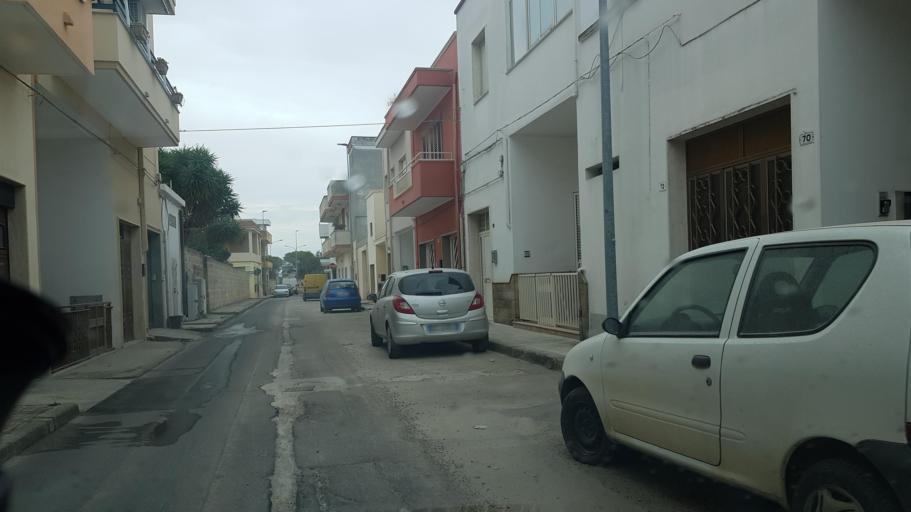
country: IT
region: Apulia
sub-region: Provincia di Lecce
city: Leverano
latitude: 40.2863
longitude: 17.9991
